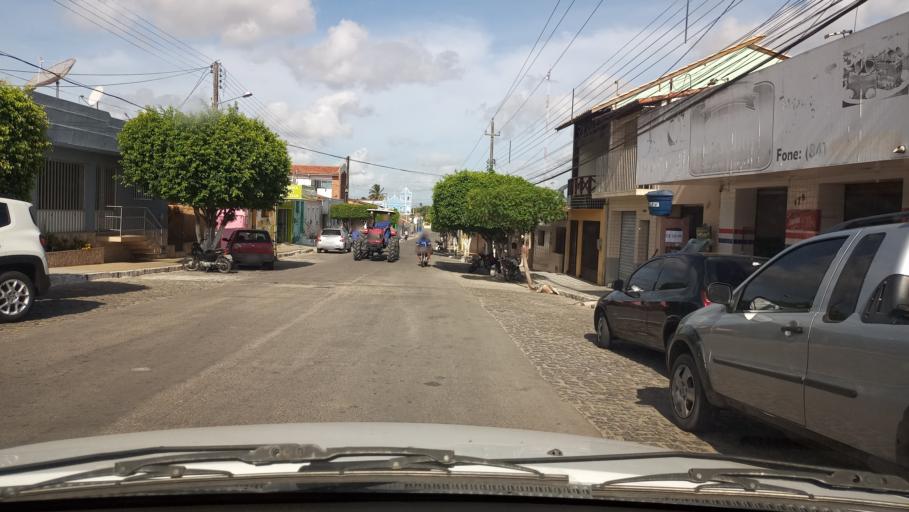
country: BR
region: Rio Grande do Norte
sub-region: Goianinha
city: Goianinha
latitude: -6.3321
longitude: -35.3093
